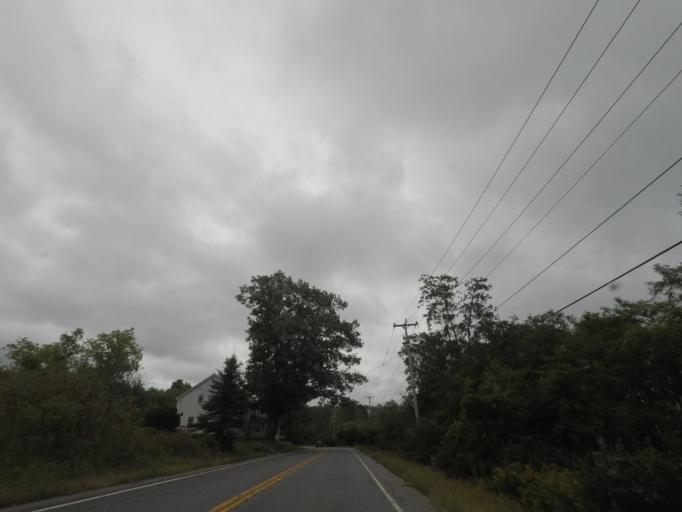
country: US
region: New York
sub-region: Saratoga County
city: Country Knolls
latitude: 42.9331
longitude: -73.7679
